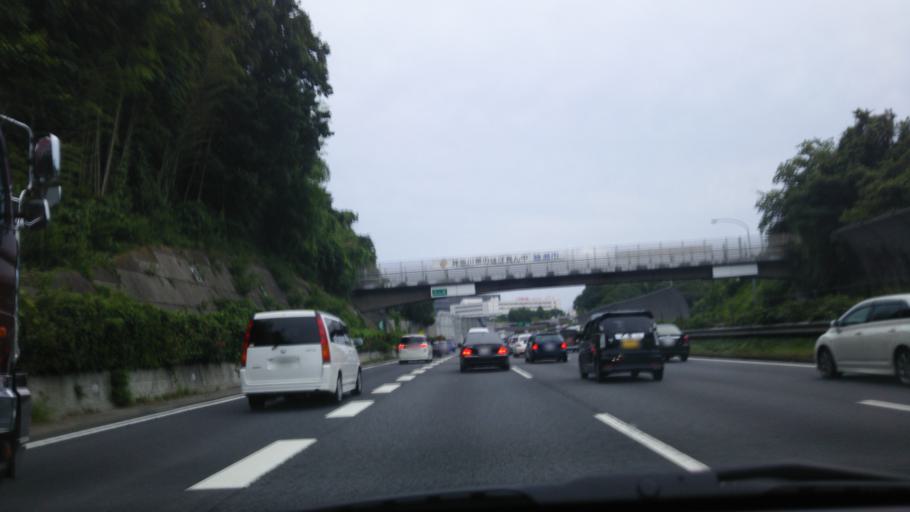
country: JP
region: Kanagawa
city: Atsugi
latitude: 35.4415
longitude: 139.4083
